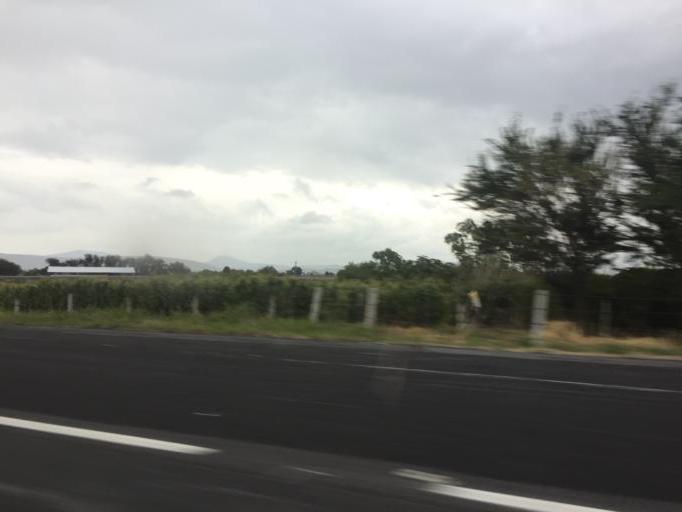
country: MX
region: Jalisco
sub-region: Zapotlan del Rey
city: Zapotlan del Rey
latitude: 20.4677
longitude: -102.9104
